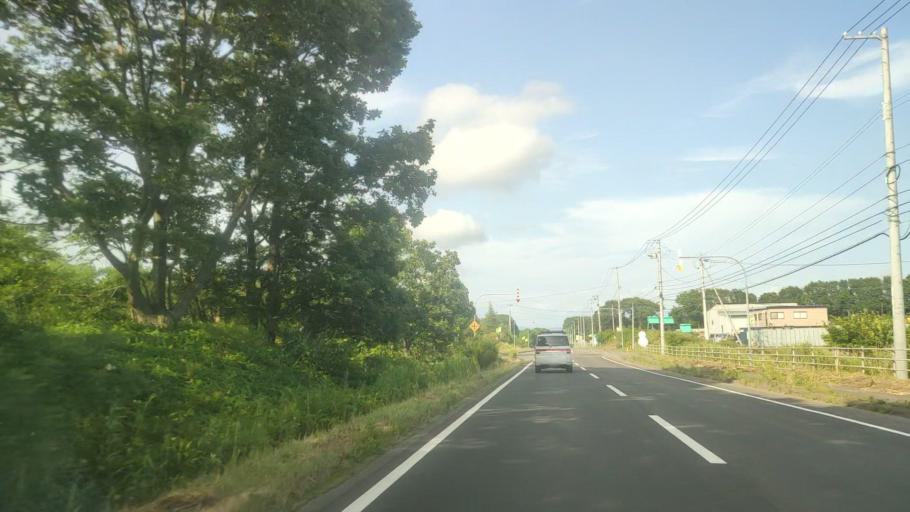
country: JP
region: Hokkaido
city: Chitose
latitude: 42.7428
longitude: 141.7865
